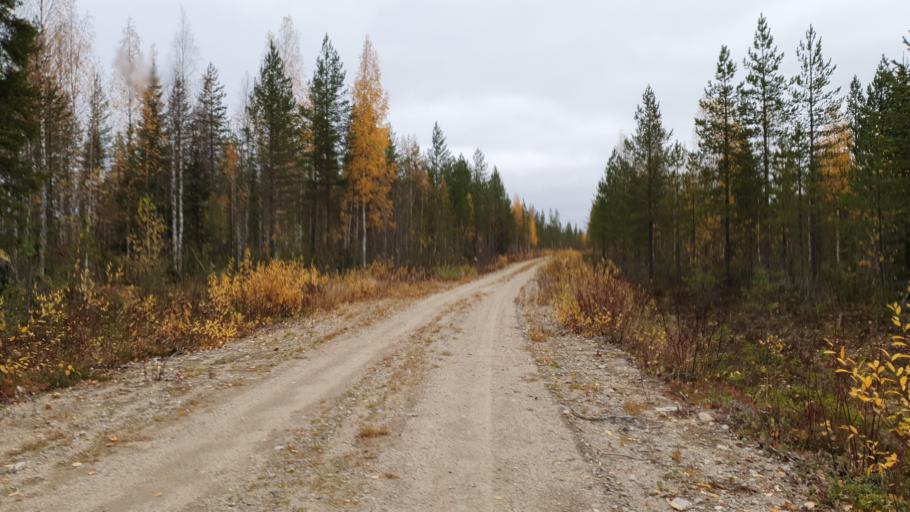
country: FI
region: Kainuu
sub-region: Kehys-Kainuu
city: Kuhmo
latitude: 64.4406
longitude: 29.6193
